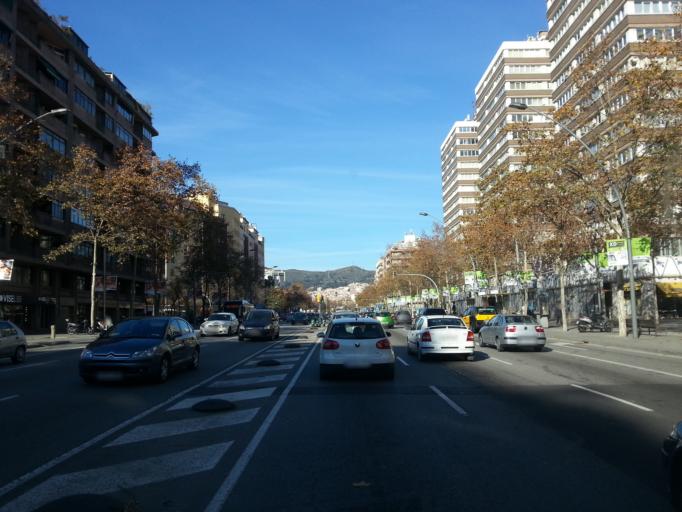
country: ES
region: Catalonia
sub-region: Provincia de Barcelona
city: Sant Andreu de Palomar
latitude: 41.4271
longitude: 2.1853
